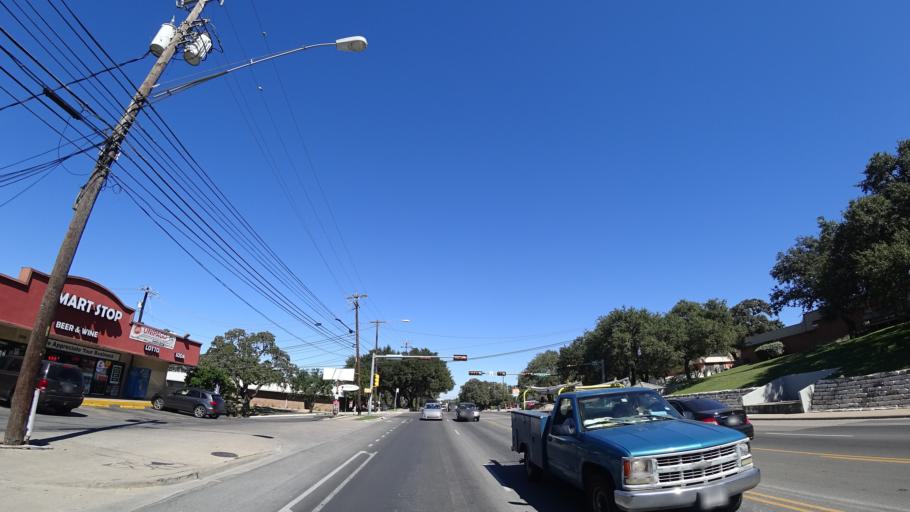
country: US
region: Texas
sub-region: Travis County
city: Austin
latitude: 30.2352
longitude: -97.7567
